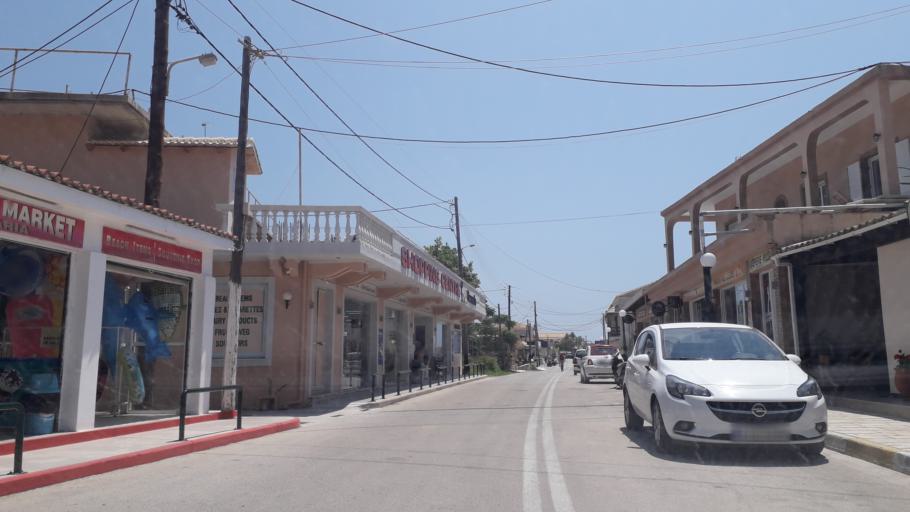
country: GR
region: Ionian Islands
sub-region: Nomos Kerkyras
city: Perivoli
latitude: 39.4276
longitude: 19.9429
